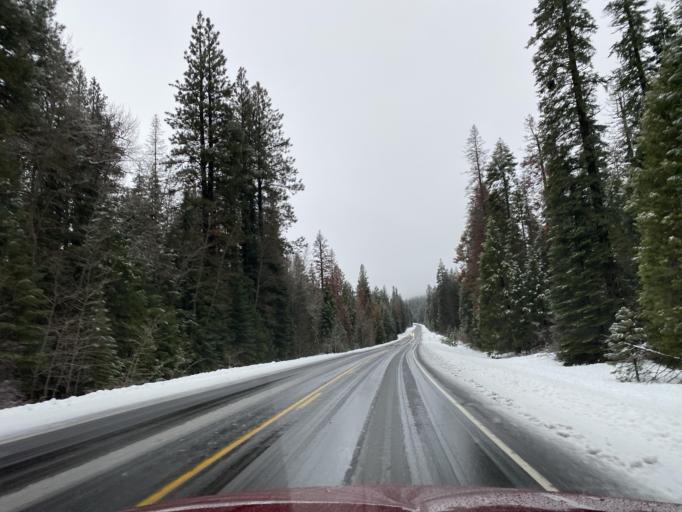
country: US
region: Oregon
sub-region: Klamath County
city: Klamath Falls
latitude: 42.5479
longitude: -122.0865
